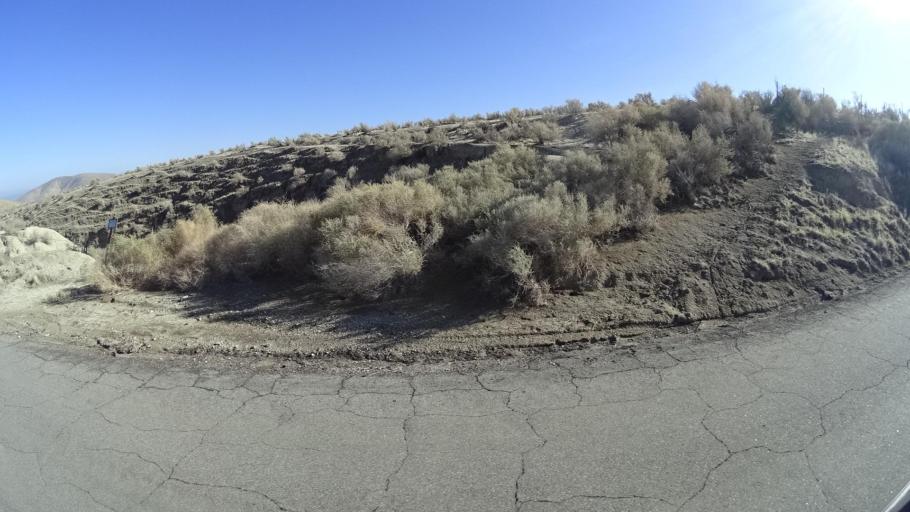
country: US
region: California
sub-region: Kern County
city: Maricopa
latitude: 34.9899
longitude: -119.3921
